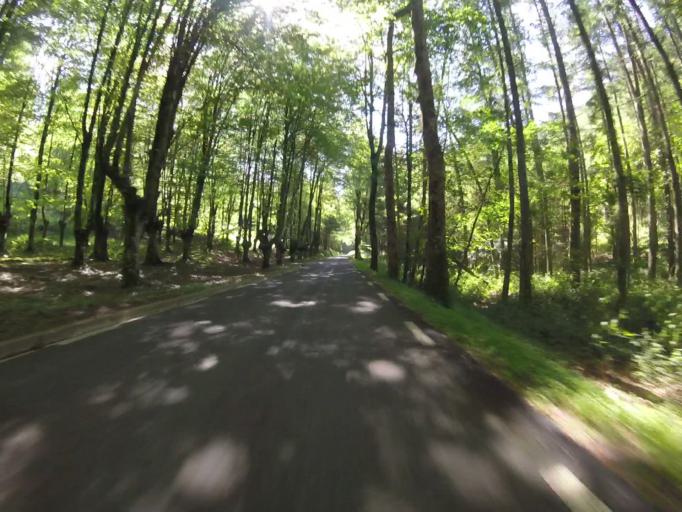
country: ES
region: Basque Country
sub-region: Provincia de Guipuzcoa
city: Albiztur
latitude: 43.1224
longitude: -2.1652
